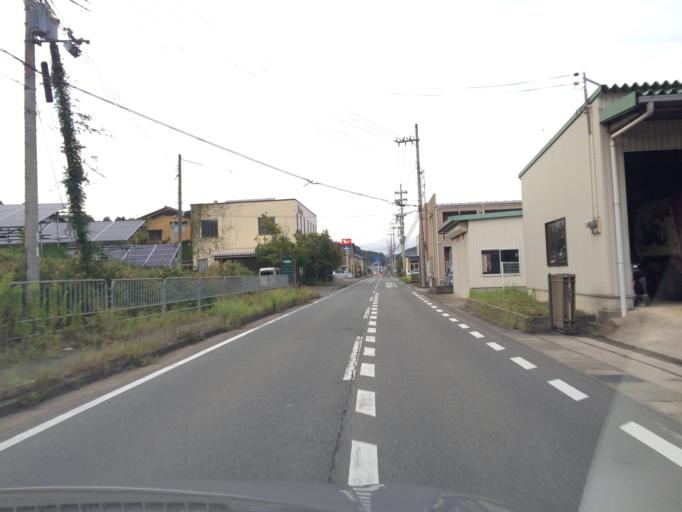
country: JP
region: Hyogo
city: Toyooka
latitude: 35.5247
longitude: 134.8178
